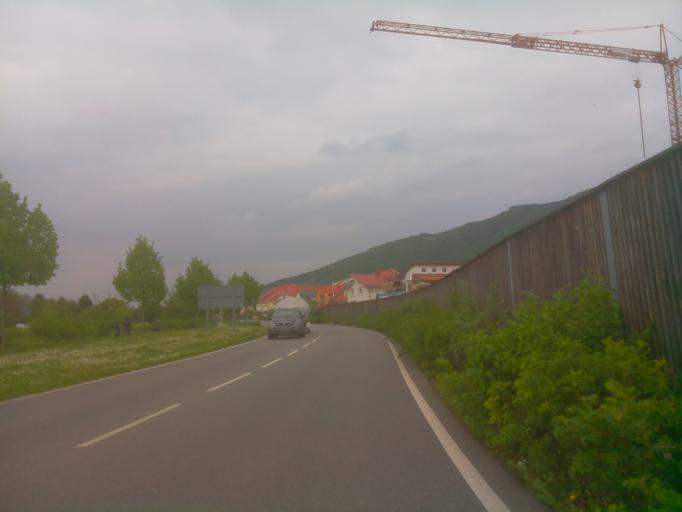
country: DE
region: Baden-Wuerttemberg
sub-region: Karlsruhe Region
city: Dossenheim
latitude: 49.4519
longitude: 8.6632
